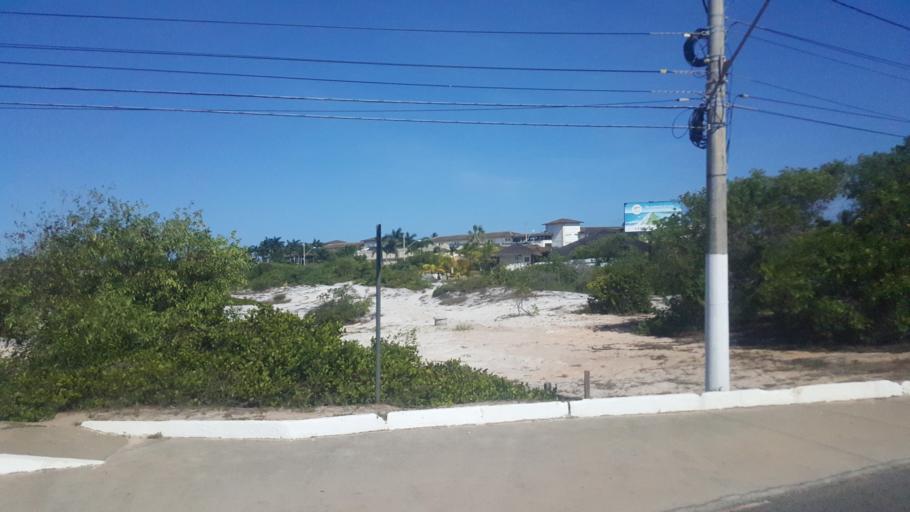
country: BR
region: Bahia
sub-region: Mata De Sao Joao
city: Mata de Sao Joao
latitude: -12.4385
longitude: -37.9230
